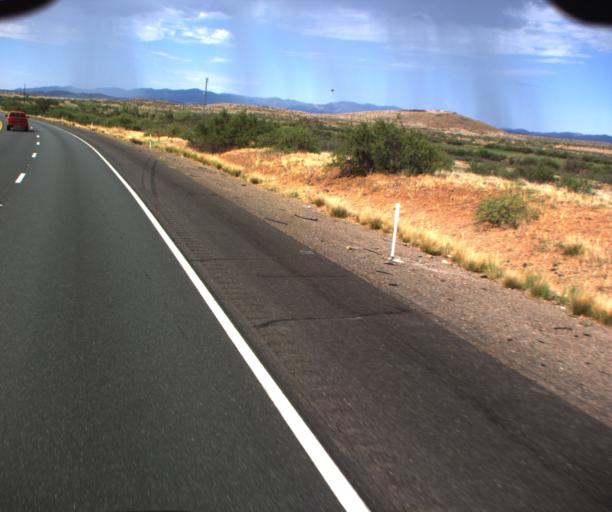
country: US
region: Arizona
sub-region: Yavapai County
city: Cordes Lakes
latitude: 34.4117
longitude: -112.0699
